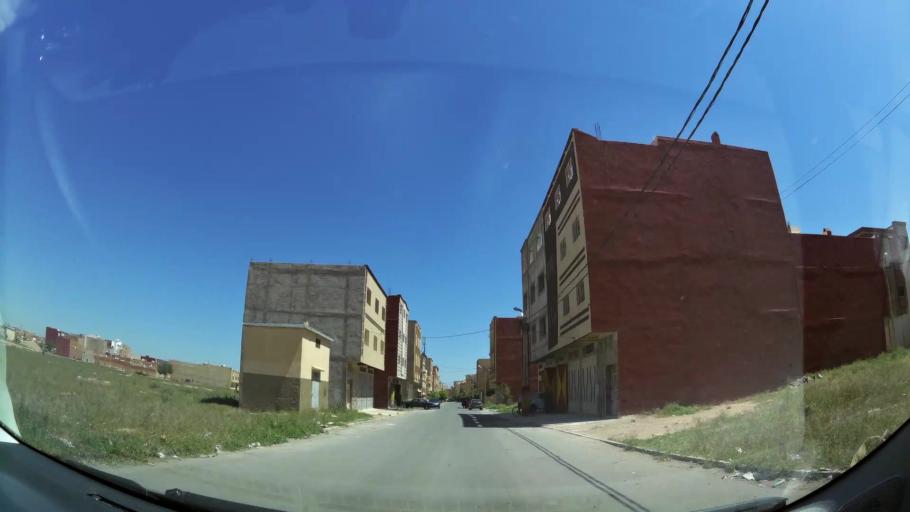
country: MA
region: Oriental
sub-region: Oujda-Angad
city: Oujda
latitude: 34.6691
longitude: -1.8928
